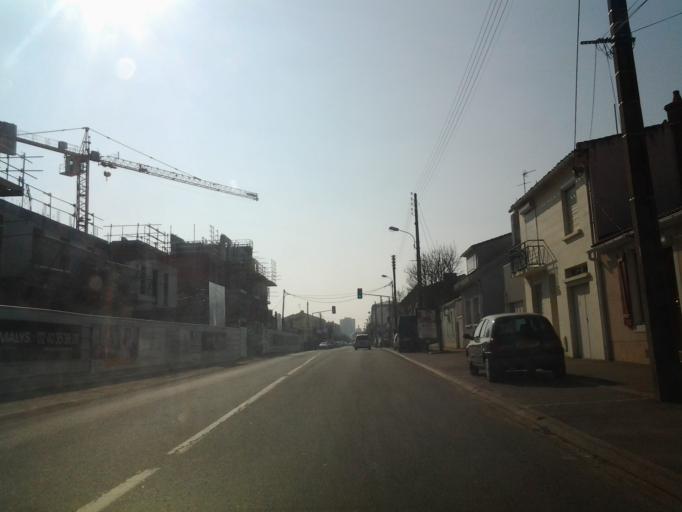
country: FR
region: Pays de la Loire
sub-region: Departement de la Vendee
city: Les Sables-d'Olonne
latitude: 46.5047
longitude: -1.7732
